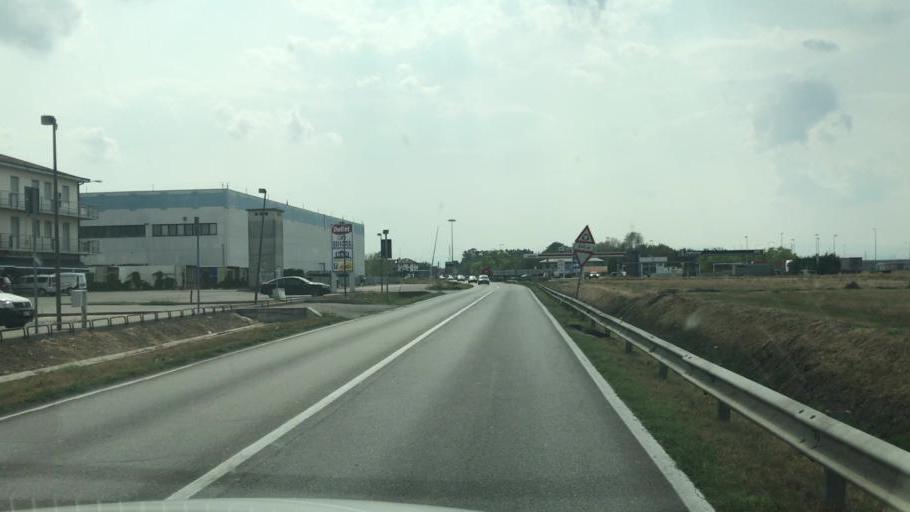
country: IT
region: Emilia-Romagna
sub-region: Provincia di Parma
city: Baganzola
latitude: 44.8512
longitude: 10.3419
